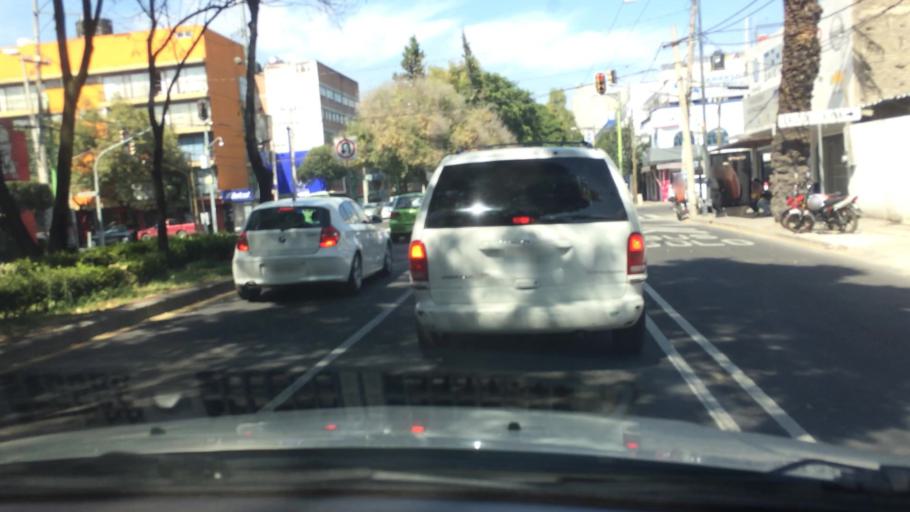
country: MX
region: Mexico City
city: Coyoacan
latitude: 19.3451
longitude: -99.1495
